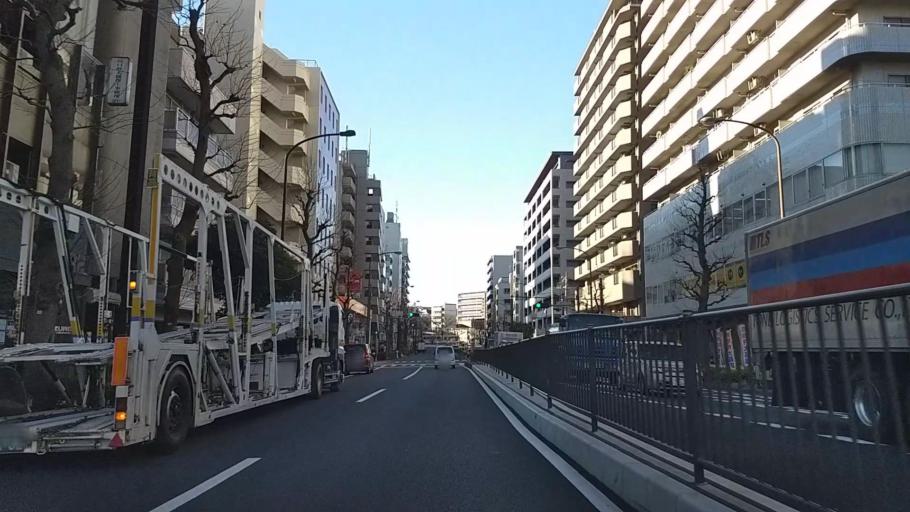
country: JP
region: Kanagawa
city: Yokohama
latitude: 35.4770
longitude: 139.6284
